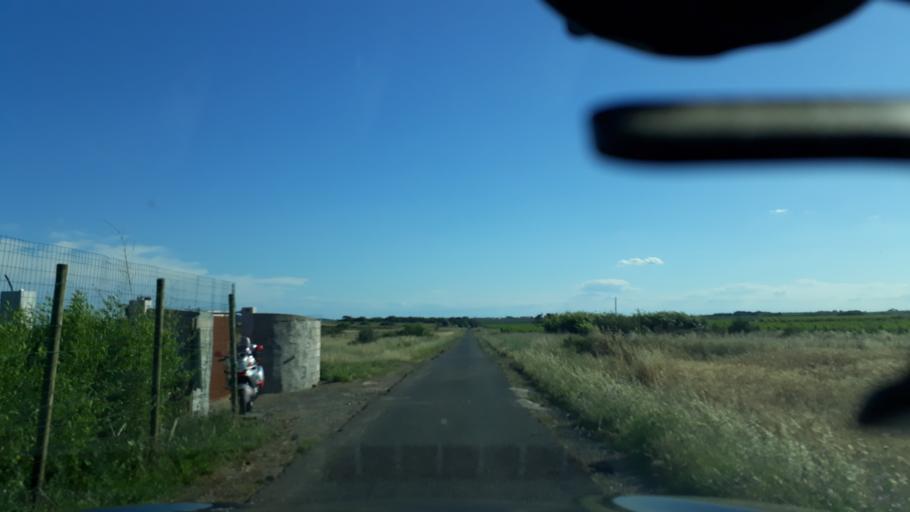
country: FR
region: Languedoc-Roussillon
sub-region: Departement de l'Herault
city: Marseillan
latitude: 43.3441
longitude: 3.5128
